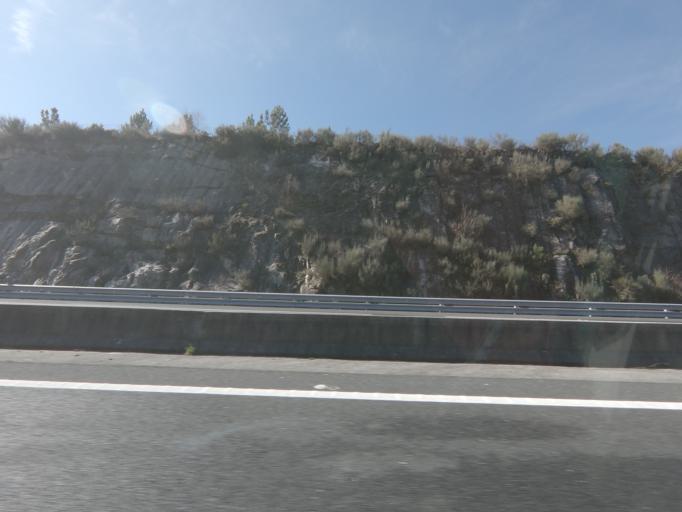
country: ES
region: Galicia
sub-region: Provincia de Ourense
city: Pinor
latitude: 42.4995
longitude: -8.0285
